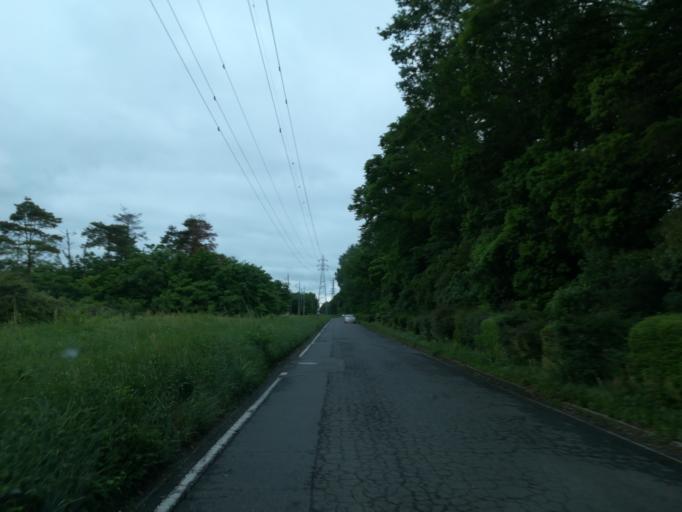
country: JP
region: Ibaraki
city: Tsukuba
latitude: 36.1152
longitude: 140.0926
